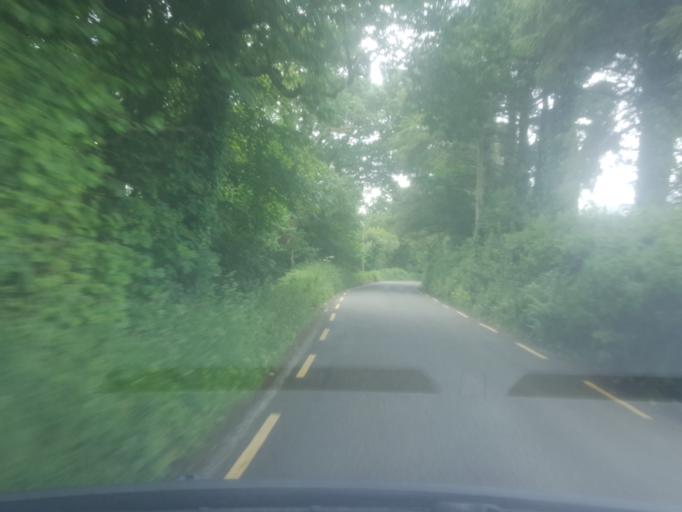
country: IE
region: Munster
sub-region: Ciarrai
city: Cill Airne
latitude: 52.0847
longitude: -9.4790
